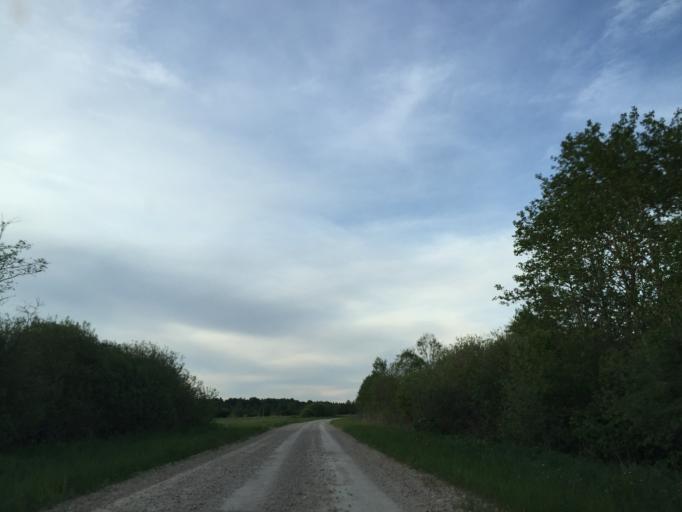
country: LV
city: Tireli
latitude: 56.7716
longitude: 23.5434
